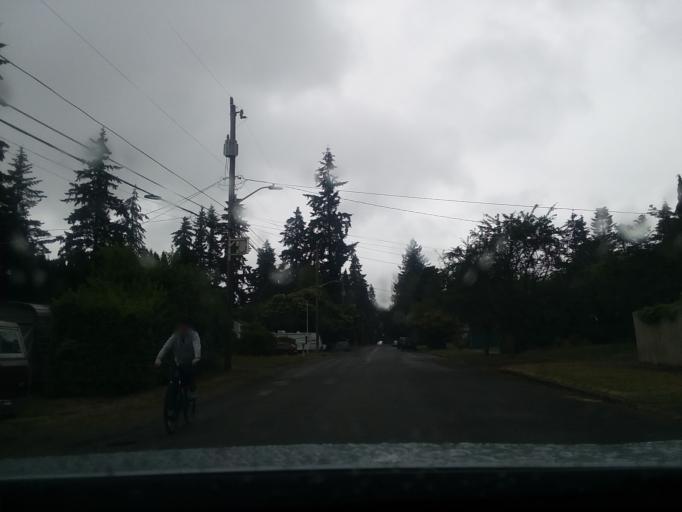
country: US
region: Washington
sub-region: King County
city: Shoreline
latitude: 47.7289
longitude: -122.3397
